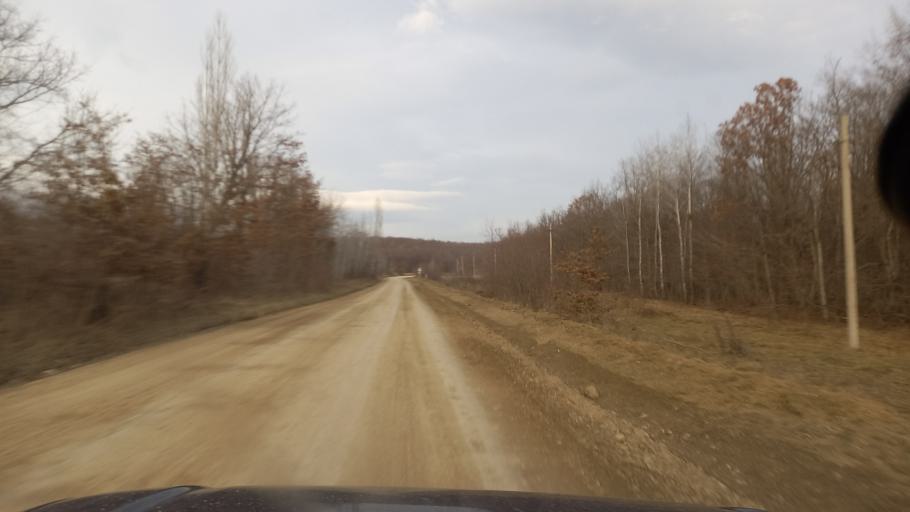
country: RU
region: Adygeya
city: Kamennomostskiy
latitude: 44.1708
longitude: 40.2466
